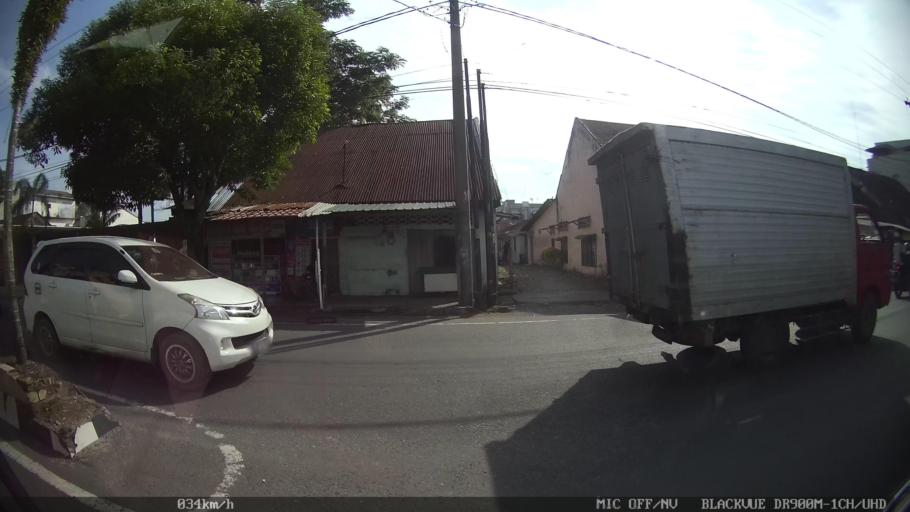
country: ID
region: North Sumatra
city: Medan
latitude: 3.5992
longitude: 98.6632
